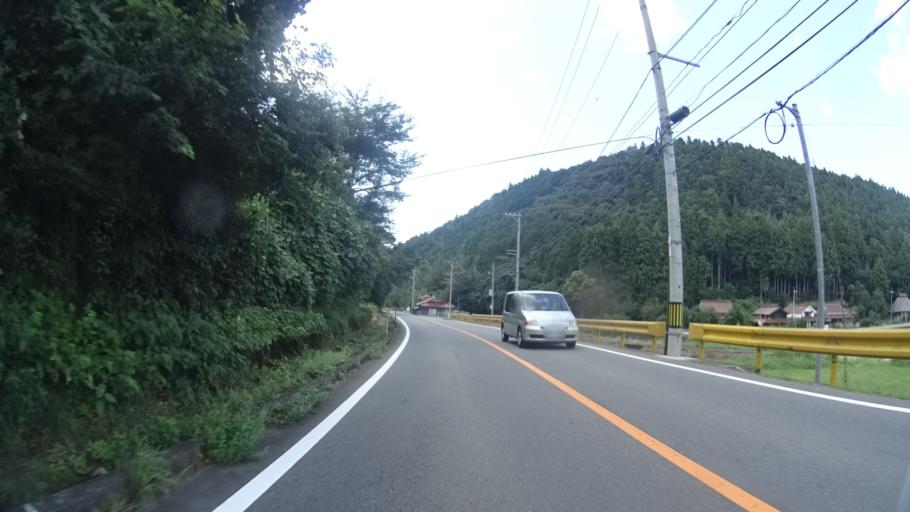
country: JP
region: Yamaguchi
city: Hagi
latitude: 34.4372
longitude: 131.4627
